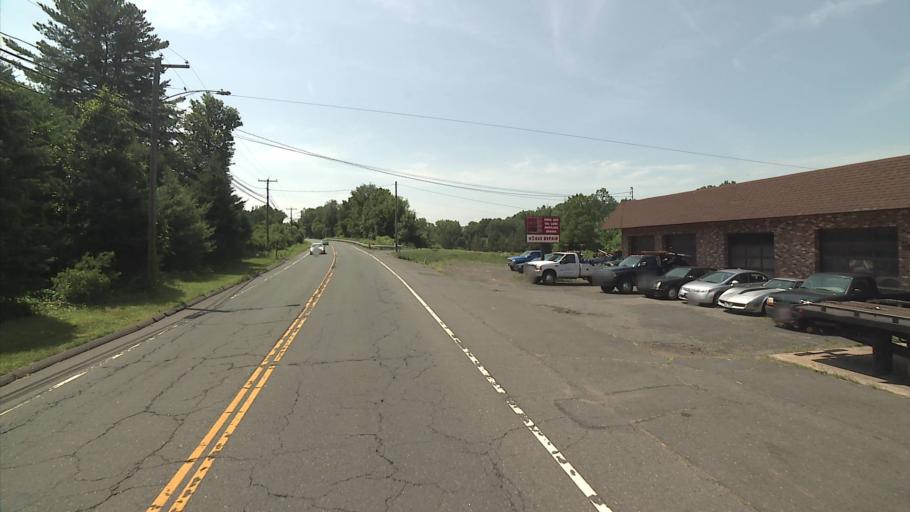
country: US
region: Connecticut
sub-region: Hartford County
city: Kensington
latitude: 41.5987
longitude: -72.7986
